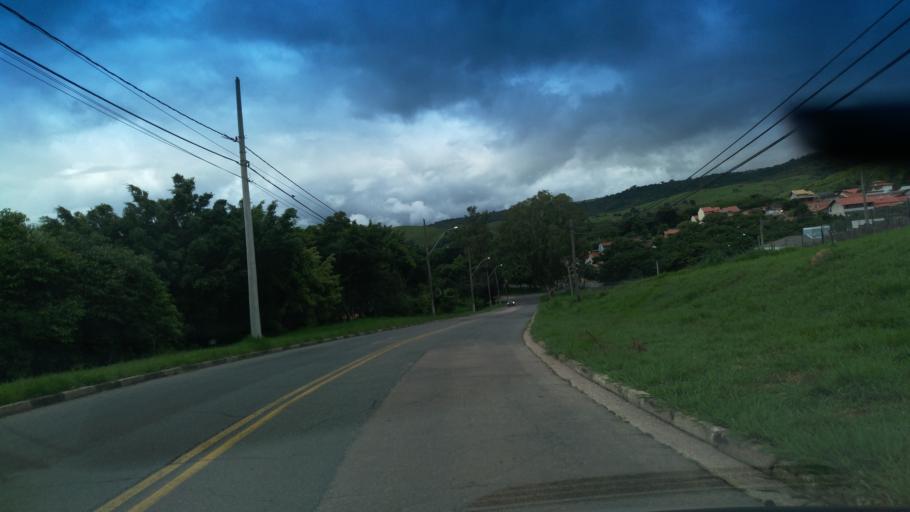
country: BR
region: Sao Paulo
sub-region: Valinhos
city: Valinhos
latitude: -22.9662
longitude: -46.9801
